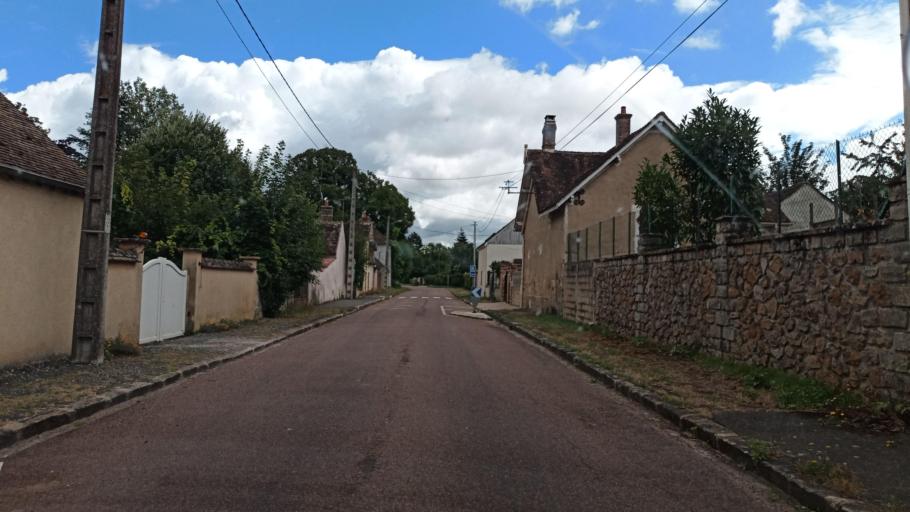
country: FR
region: Ile-de-France
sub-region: Departement de Seine-et-Marne
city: Voulx
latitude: 48.2667
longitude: 3.0043
